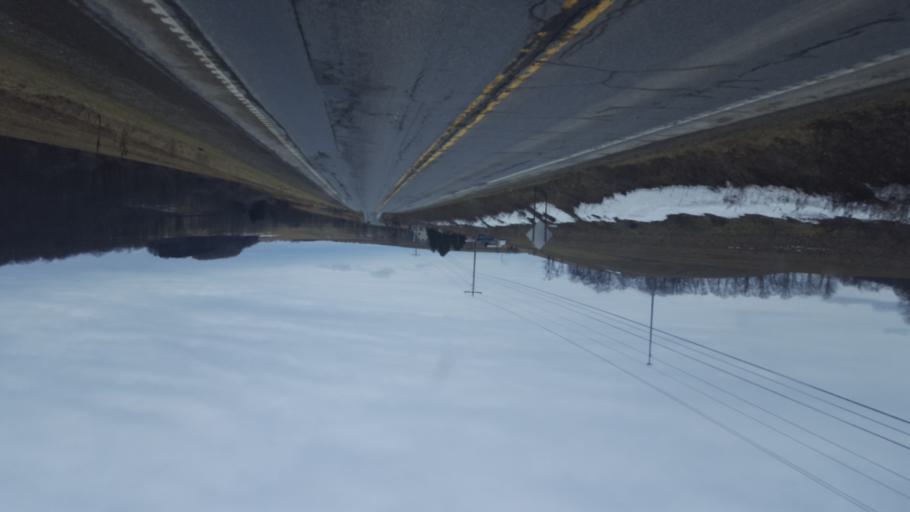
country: US
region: Pennsylvania
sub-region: Potter County
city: Coudersport
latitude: 41.8378
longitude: -77.8955
